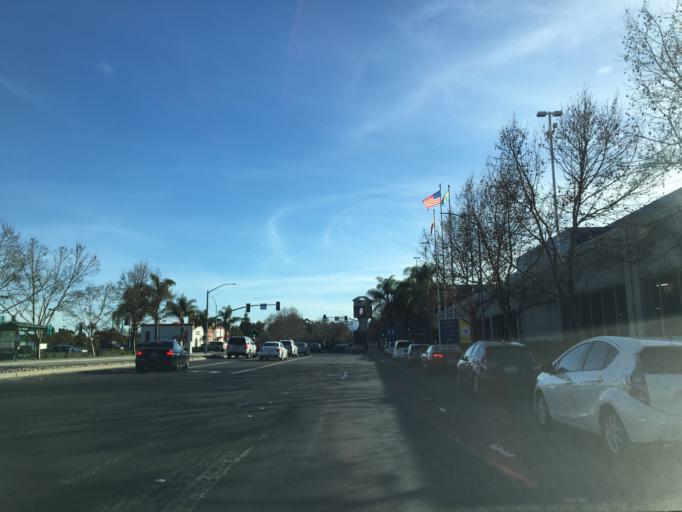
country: US
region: California
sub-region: San Mateo County
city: East Palo Alto
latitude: 37.4616
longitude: -122.1383
